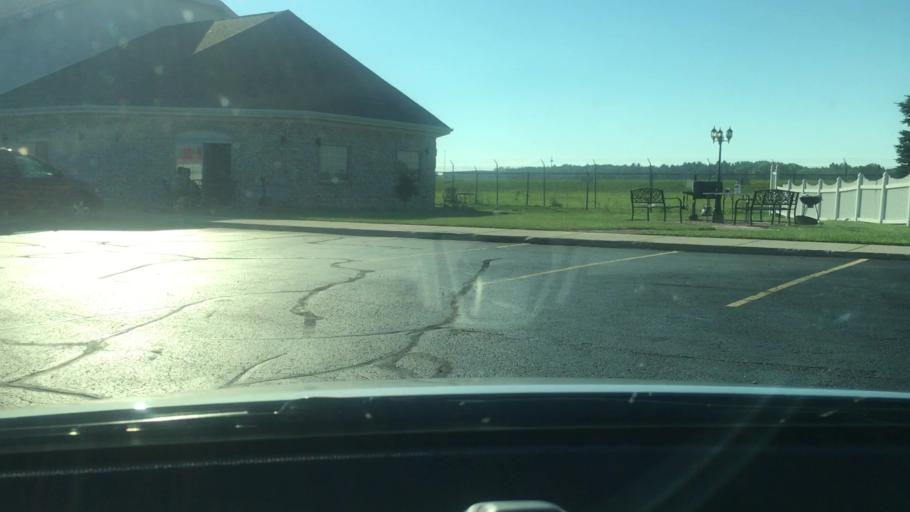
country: US
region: Wisconsin
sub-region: Brown County
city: Ashwaubenon
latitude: 44.4923
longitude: -88.1072
